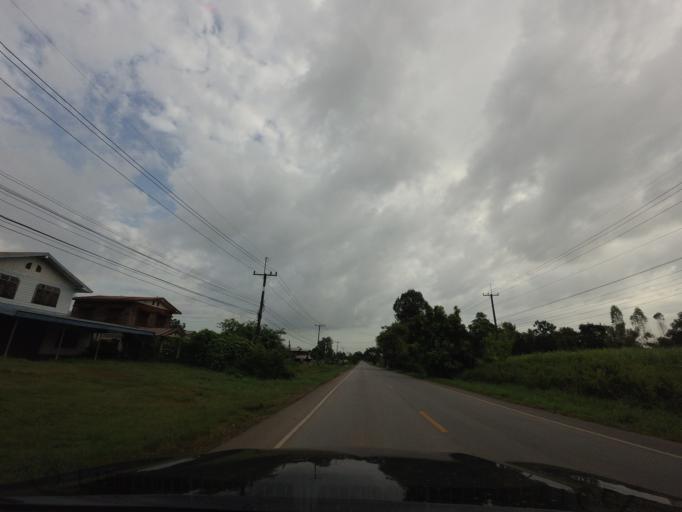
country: TH
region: Changwat Udon Thani
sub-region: Amphoe Ban Phue
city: Ban Phue
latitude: 17.7291
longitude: 102.3954
